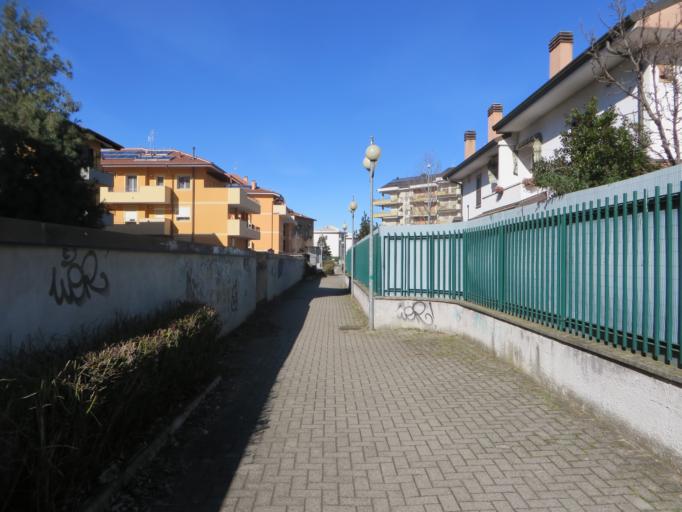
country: IT
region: Lombardy
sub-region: Citta metropolitana di Milano
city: Cornaredo
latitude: 45.4894
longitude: 9.0230
